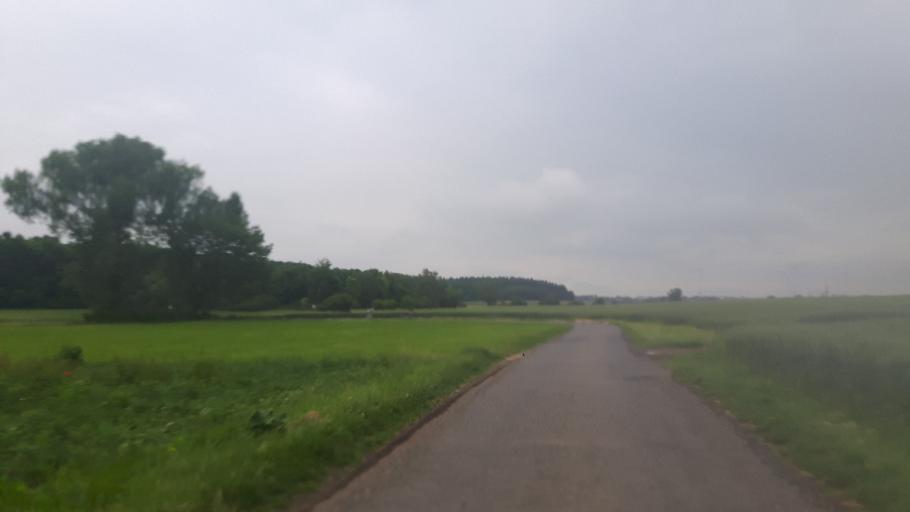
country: DE
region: Bavaria
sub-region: Regierungsbezirk Unterfranken
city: Oberpleichfeld
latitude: 49.8894
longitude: 10.1037
